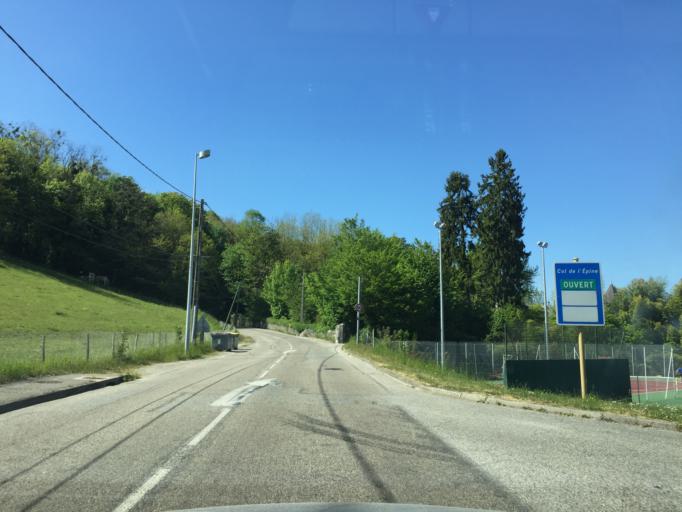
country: FR
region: Rhone-Alpes
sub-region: Departement de la Savoie
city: Cognin
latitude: 45.5632
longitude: 5.8902
